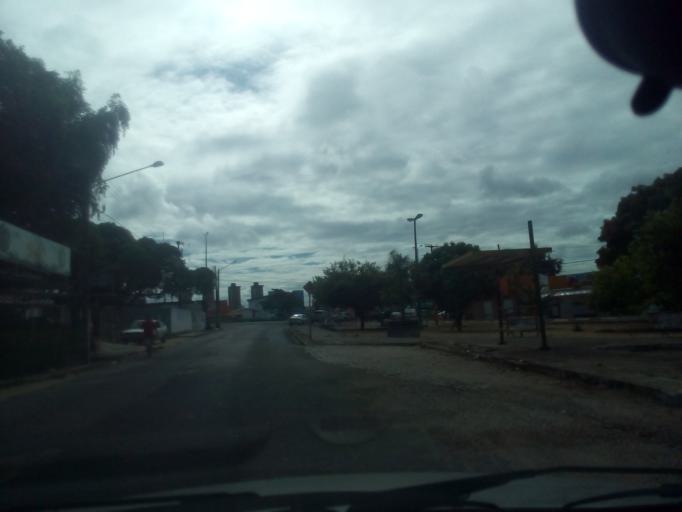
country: BR
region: Rio Grande do Norte
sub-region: Parnamirim
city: Parnamirim
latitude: -5.8714
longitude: -35.2024
